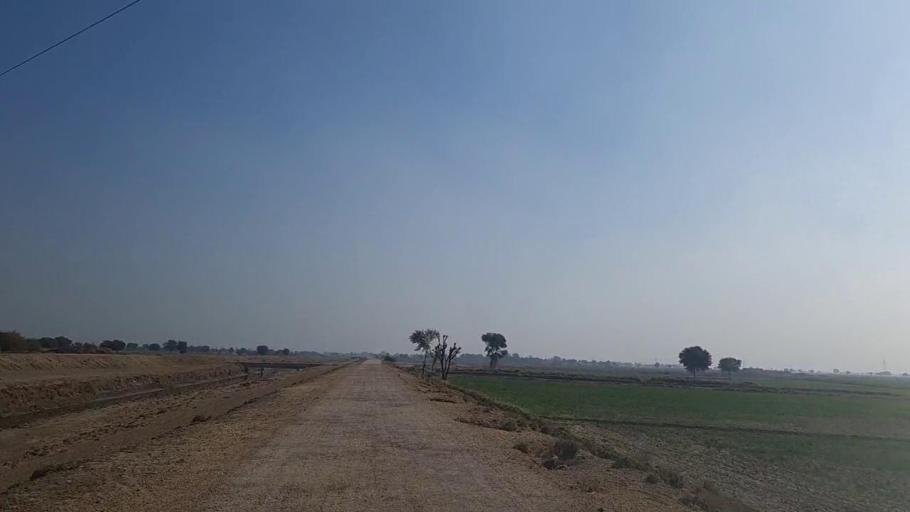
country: PK
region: Sindh
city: Shahpur Chakar
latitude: 26.1887
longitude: 68.5562
